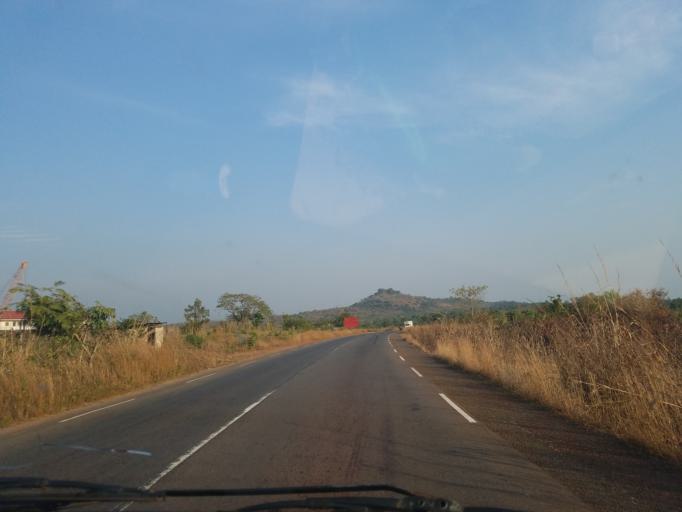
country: GN
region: Boke
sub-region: Boffa
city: Boffa
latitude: 10.3513
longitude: -14.2521
